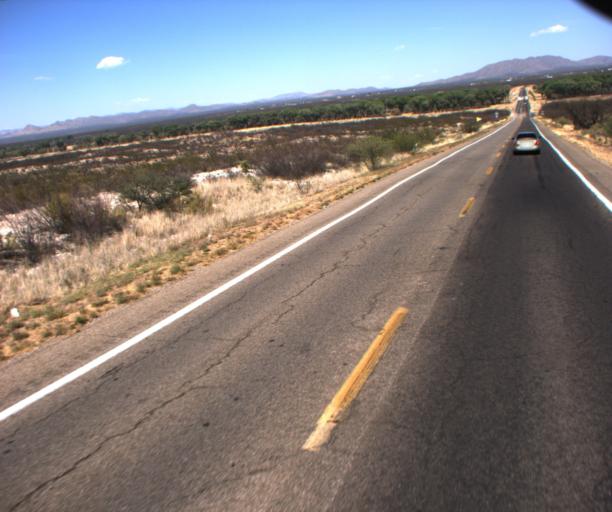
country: US
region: Arizona
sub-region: Cochise County
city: Sierra Vista Southeast
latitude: 31.5486
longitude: -110.1483
